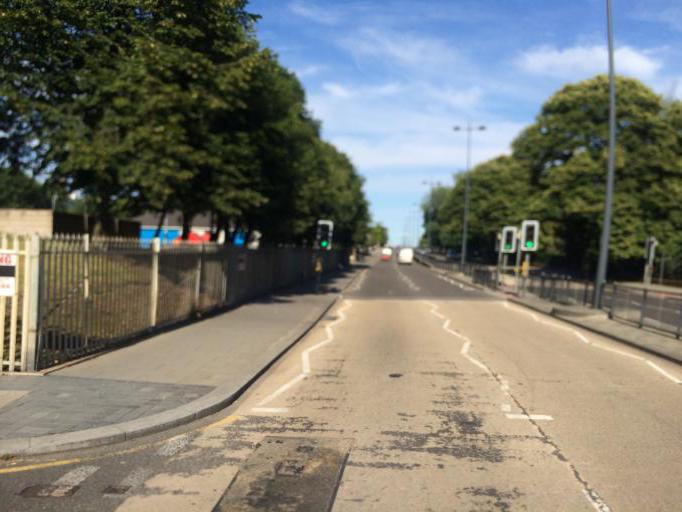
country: GB
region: England
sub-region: Liverpool
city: Liverpool
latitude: 53.4084
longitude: -2.9433
